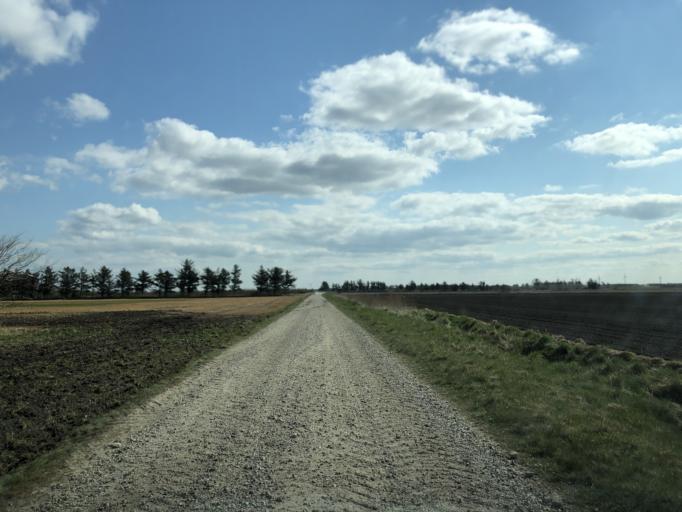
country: DK
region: Central Jutland
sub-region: Lemvig Kommune
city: Lemvig
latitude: 56.4026
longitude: 8.1835
